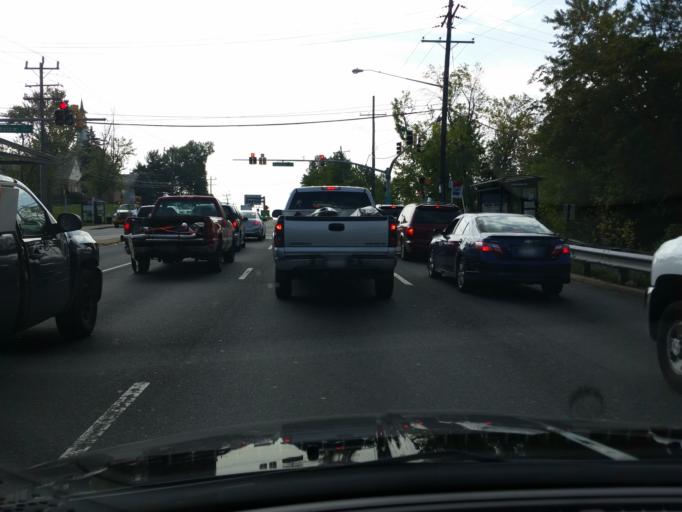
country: US
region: Maryland
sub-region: Montgomery County
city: Hillandale
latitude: 39.0158
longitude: -76.9778
